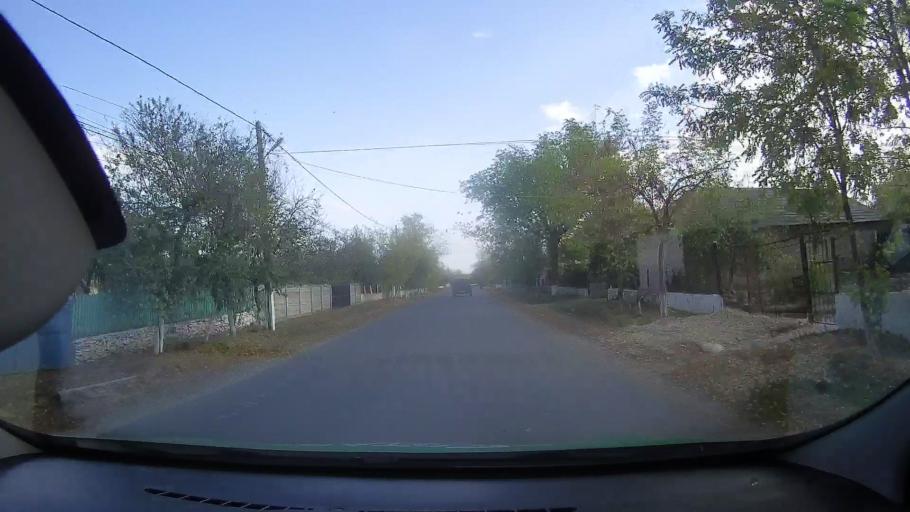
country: RO
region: Constanta
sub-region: Comuna Sacele
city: Sacele
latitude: 44.4886
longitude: 28.6377
